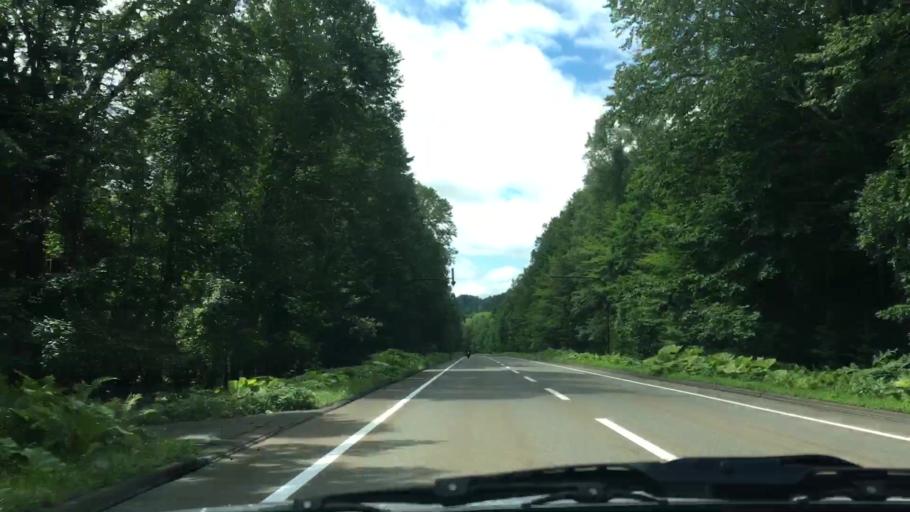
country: JP
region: Hokkaido
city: Kitami
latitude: 43.4015
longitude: 143.9301
